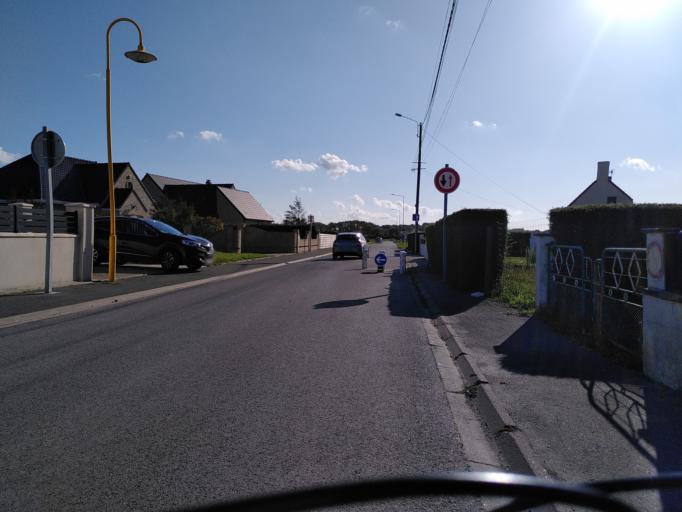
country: FR
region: Nord-Pas-de-Calais
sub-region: Departement du Pas-de-Calais
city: Marck
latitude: 50.9791
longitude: 1.9551
